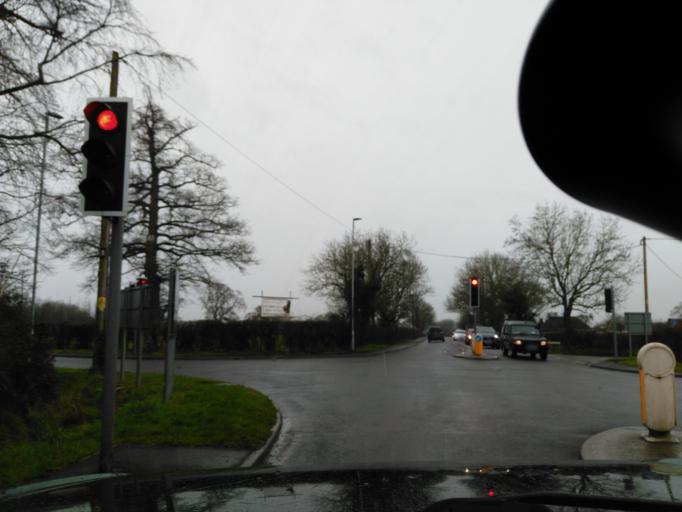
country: GB
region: England
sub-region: Wiltshire
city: Wingfield
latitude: 51.3145
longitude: -2.2574
